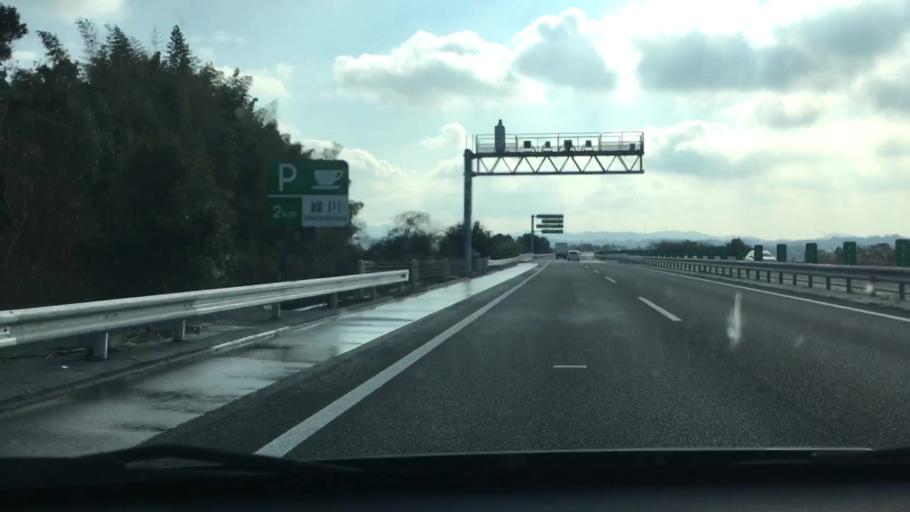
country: JP
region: Kumamoto
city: Uto
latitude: 32.7213
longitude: 130.7705
